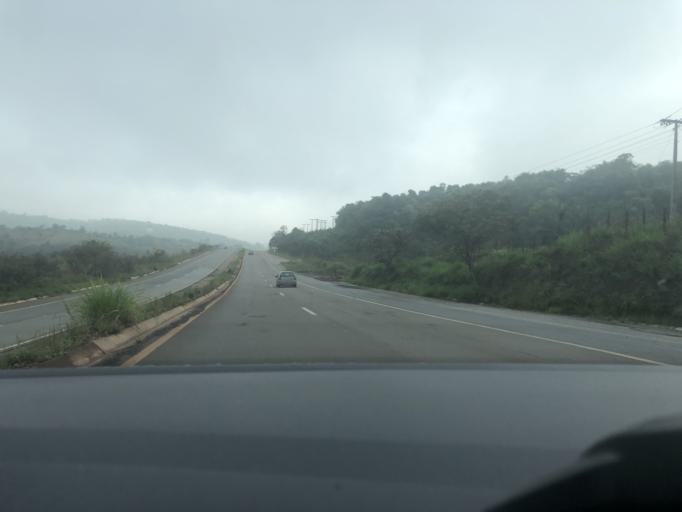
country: BR
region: Minas Gerais
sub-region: Congonhas
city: Congonhas
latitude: -20.5897
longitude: -43.9434
